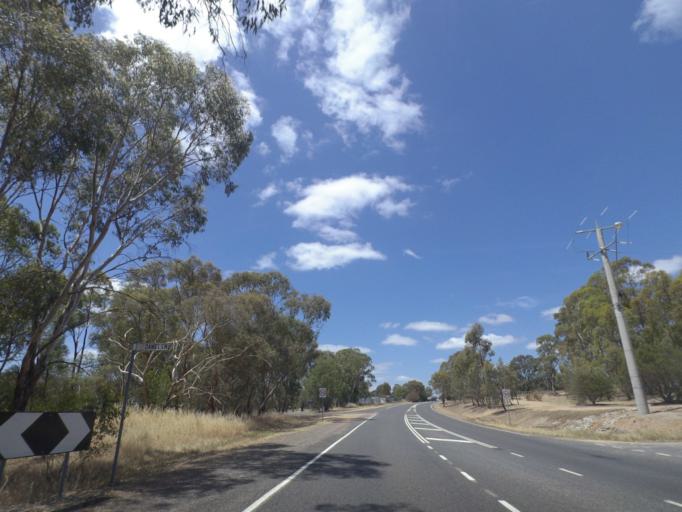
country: AU
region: Victoria
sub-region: Wangaratta
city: Wangaratta
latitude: -36.4642
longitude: 146.2171
